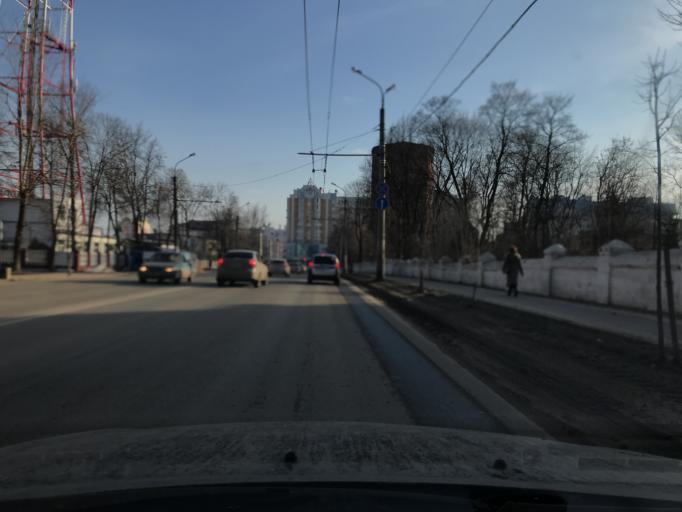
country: RU
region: Kaluga
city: Kaluga
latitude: 54.5229
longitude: 36.2603
